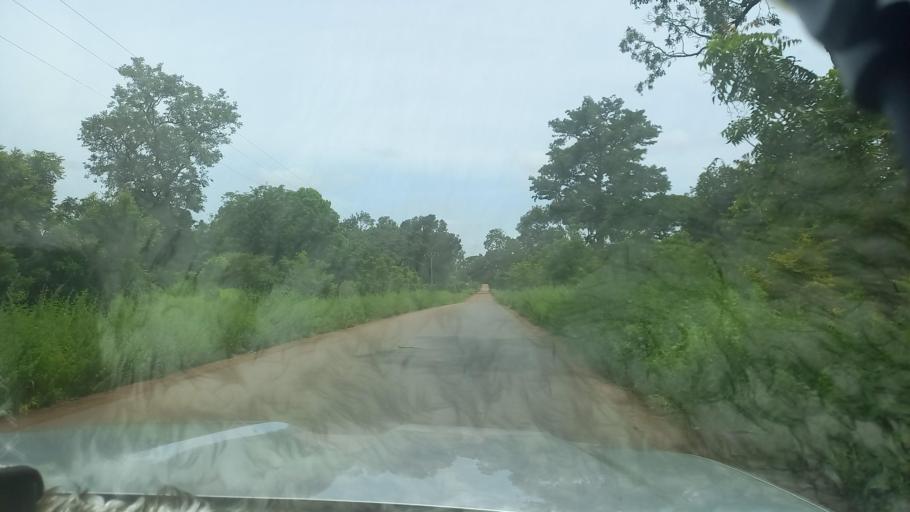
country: SN
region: Kolda
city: Marsassoum
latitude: 12.9649
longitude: -15.9704
